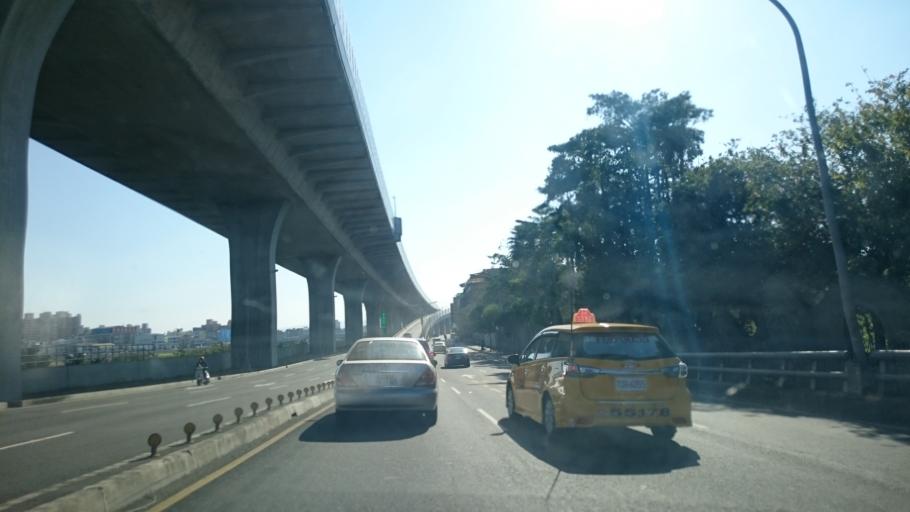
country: TW
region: Taiwan
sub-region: Taichung City
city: Taichung
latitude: 24.1002
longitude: 120.6915
